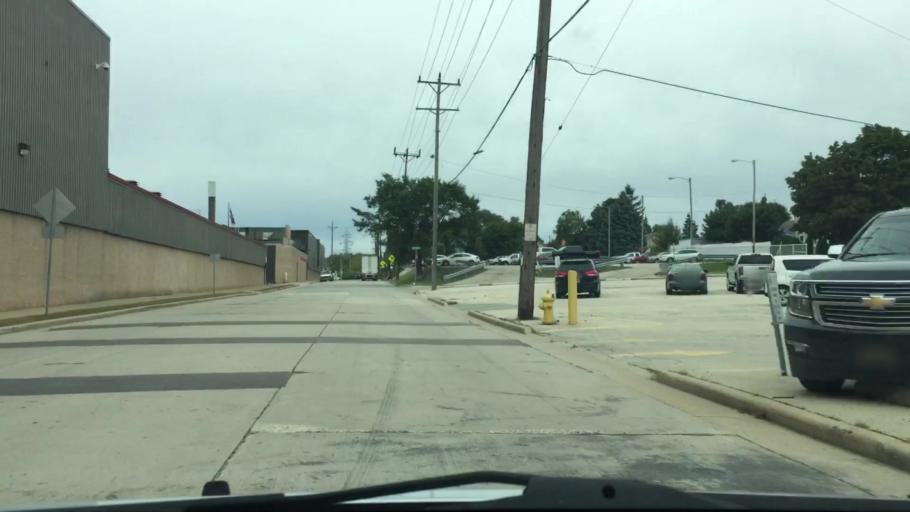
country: US
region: Wisconsin
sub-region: Waukesha County
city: Waukesha
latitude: 43.0190
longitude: -88.2178
